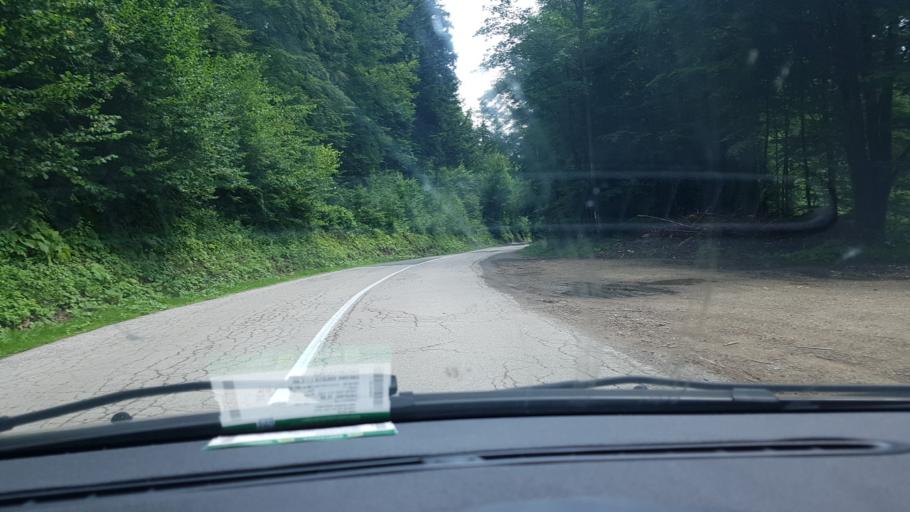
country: HR
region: Primorsko-Goranska
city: Hreljin
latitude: 45.3397
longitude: 14.6746
